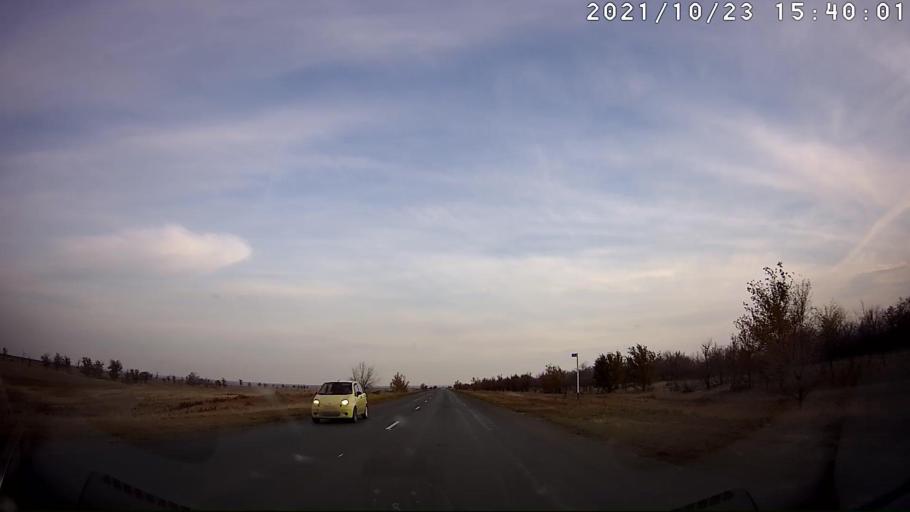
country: RU
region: Kalmykiya
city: Sadovoye
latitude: 48.1174
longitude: 44.1358
